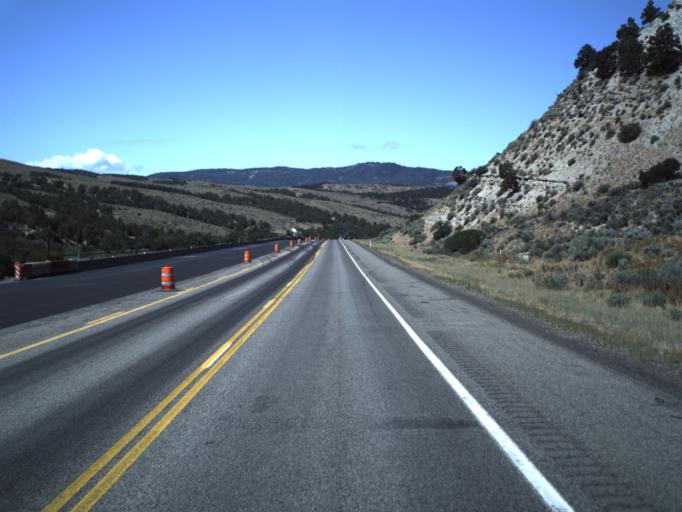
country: US
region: Utah
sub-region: Utah County
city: Mapleton
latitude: 39.9519
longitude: -111.2833
